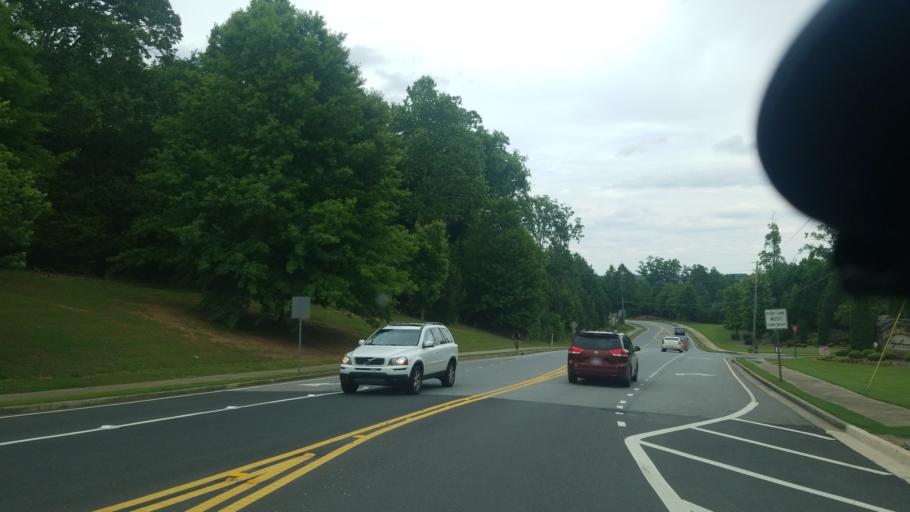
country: US
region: Georgia
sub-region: Forsyth County
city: Cumming
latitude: 34.1337
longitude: -84.1402
